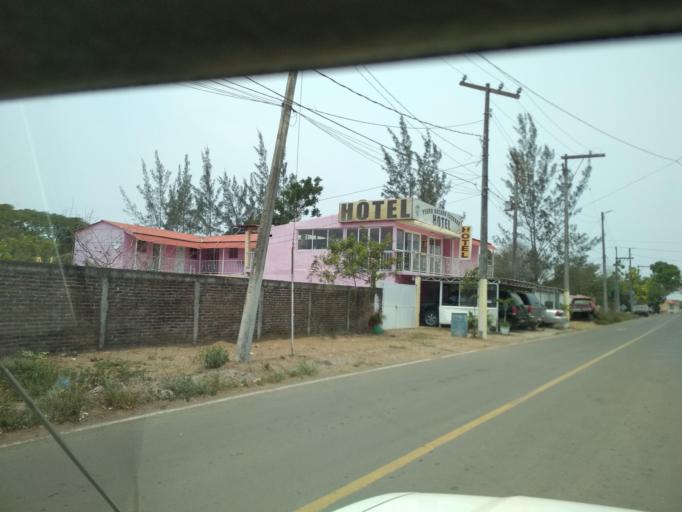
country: MX
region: Veracruz
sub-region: Veracruz
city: Delfino Victoria (Santa Fe)
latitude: 19.2100
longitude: -96.2676
